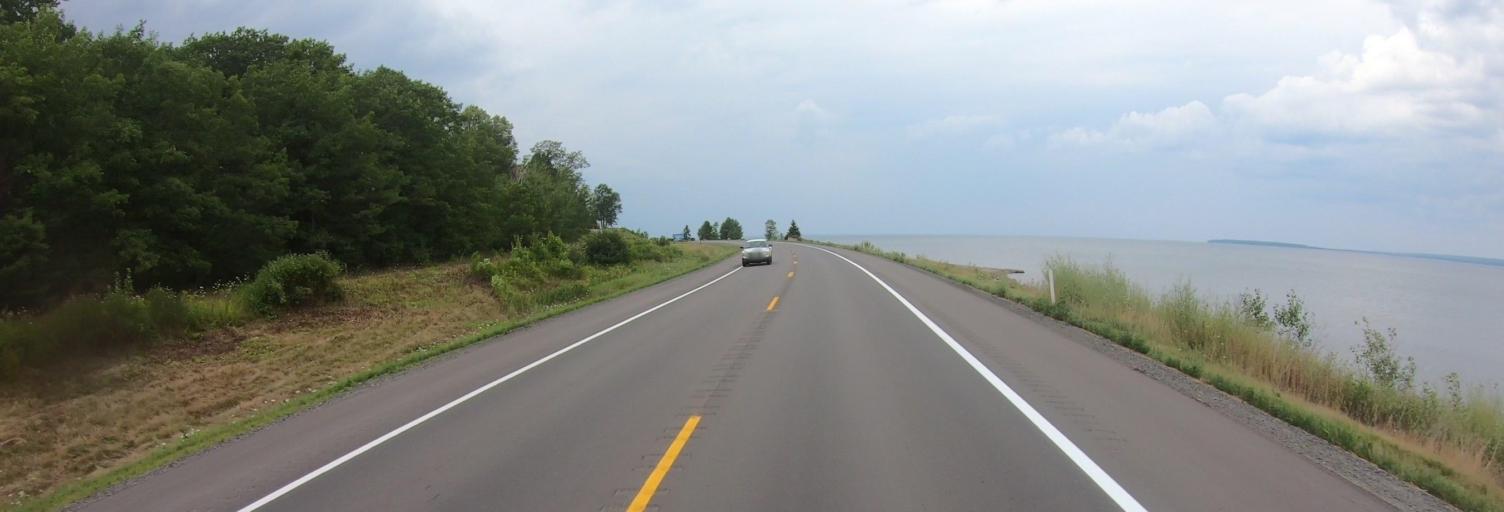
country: US
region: Michigan
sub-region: Baraga County
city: Baraga
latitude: 46.8083
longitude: -88.4743
